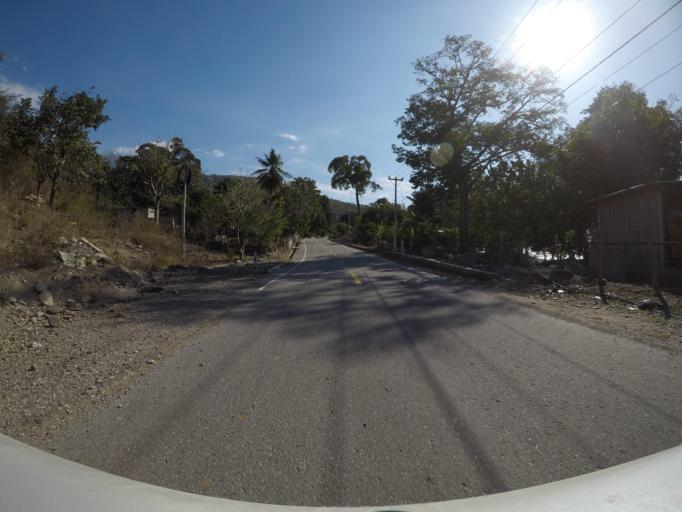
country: TL
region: Liquica
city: Maubara
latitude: -8.6361
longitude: 125.1404
